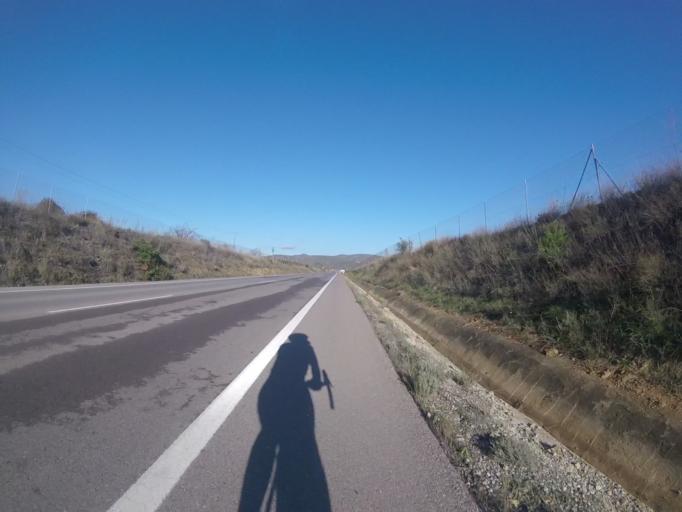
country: ES
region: Valencia
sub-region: Provincia de Castello
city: Cuevas de Vinroma
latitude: 40.3128
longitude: 0.1183
